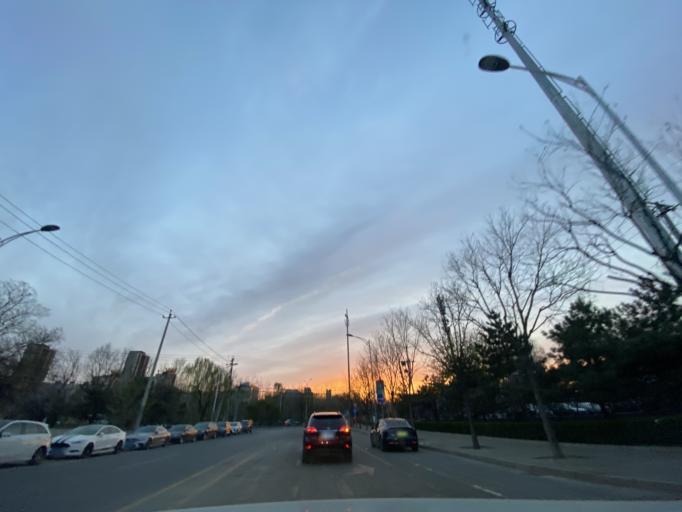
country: CN
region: Beijing
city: Qinghe
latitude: 40.0162
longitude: 116.3532
